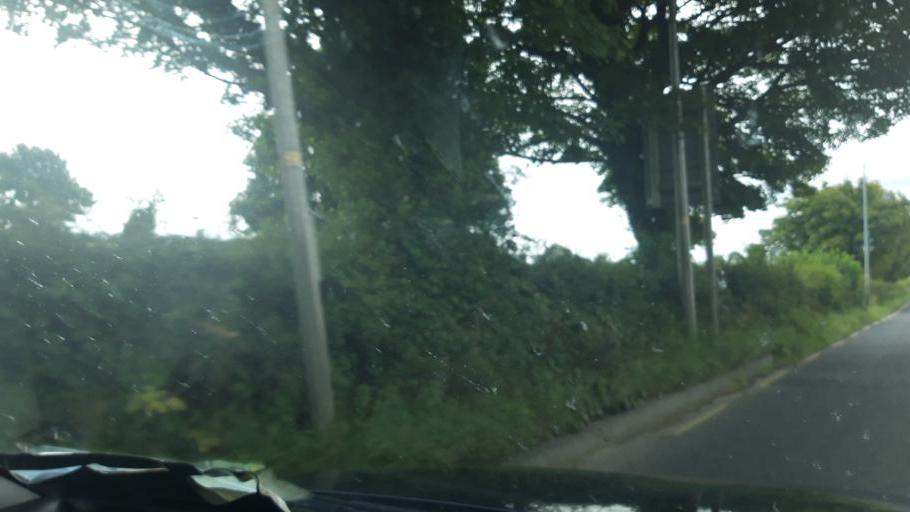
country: IE
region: Leinster
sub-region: Kilkenny
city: Callan
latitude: 52.4592
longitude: -7.4639
